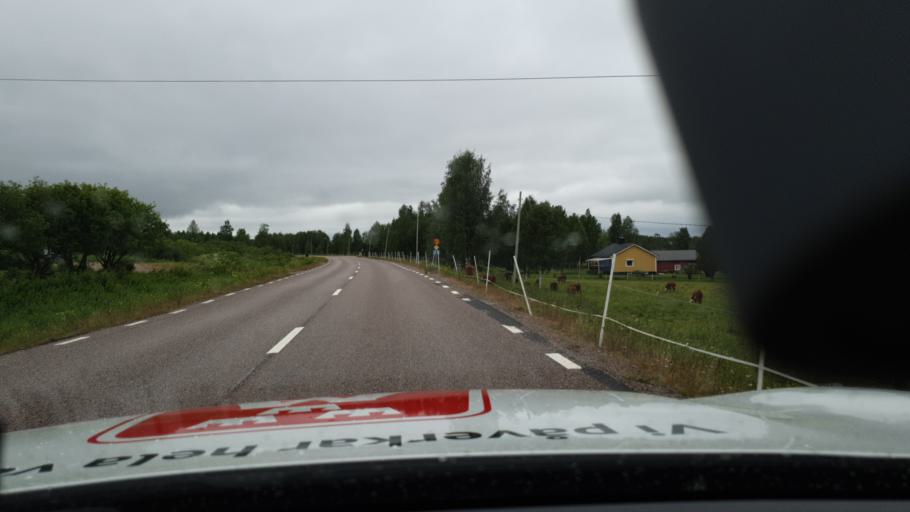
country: FI
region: Lapland
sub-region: Torniolaakso
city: Pello
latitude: 66.9535
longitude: 23.8442
